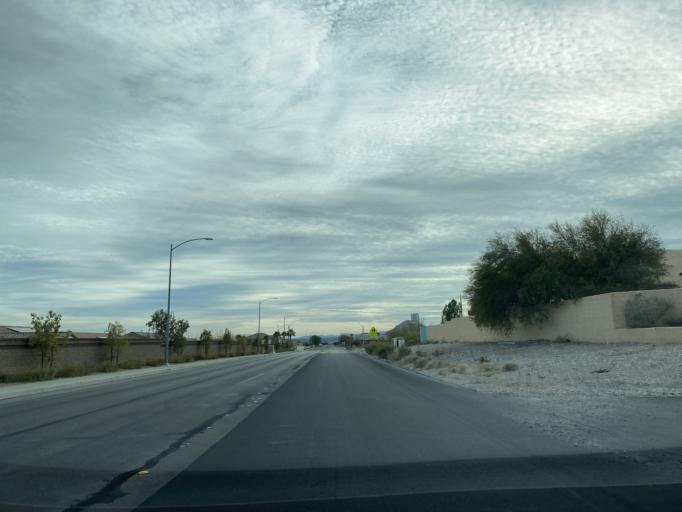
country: US
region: Nevada
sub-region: Clark County
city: Summerlin South
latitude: 36.2865
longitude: -115.3059
